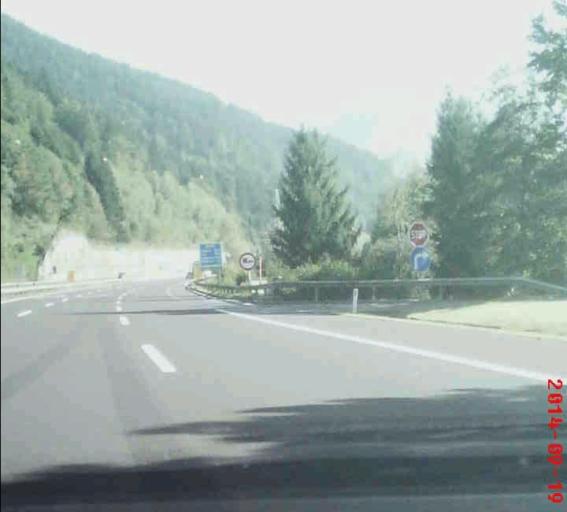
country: AT
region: Styria
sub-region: Politischer Bezirk Liezen
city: Ardning
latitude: 47.5786
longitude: 14.3195
